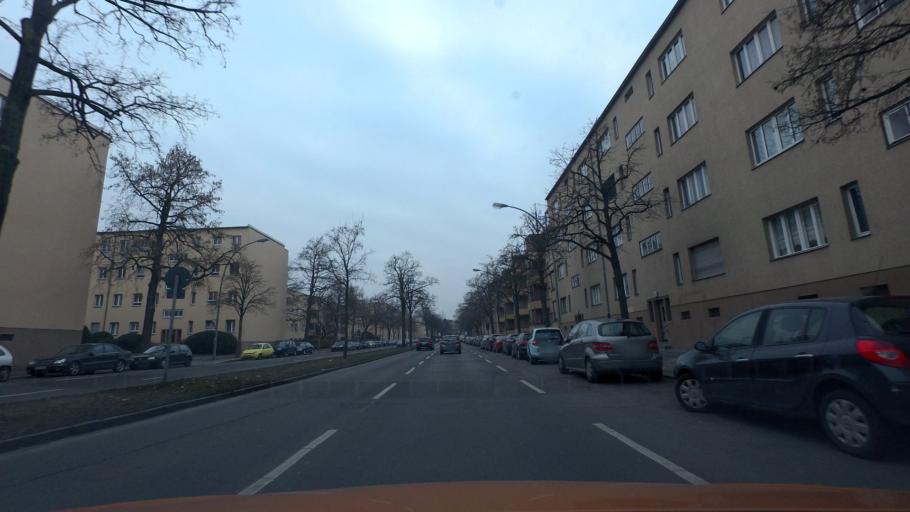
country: DE
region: Berlin
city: Schoneberg Bezirk
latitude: 52.4538
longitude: 13.3484
